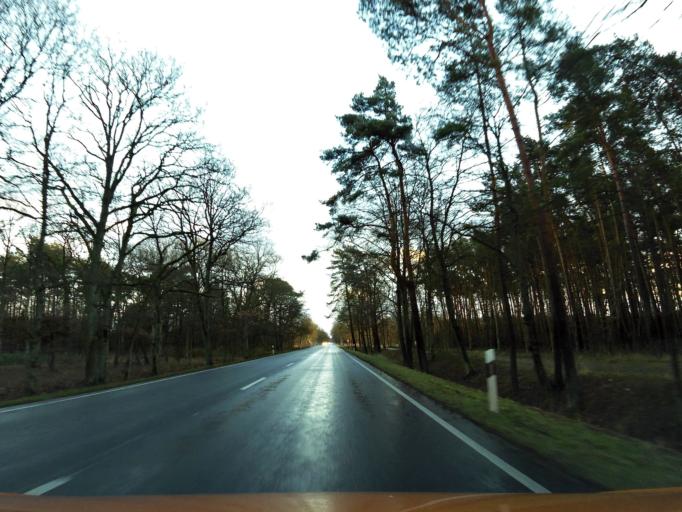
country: DE
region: Lower Saxony
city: Meinersen
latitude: 52.4643
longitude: 10.2900
